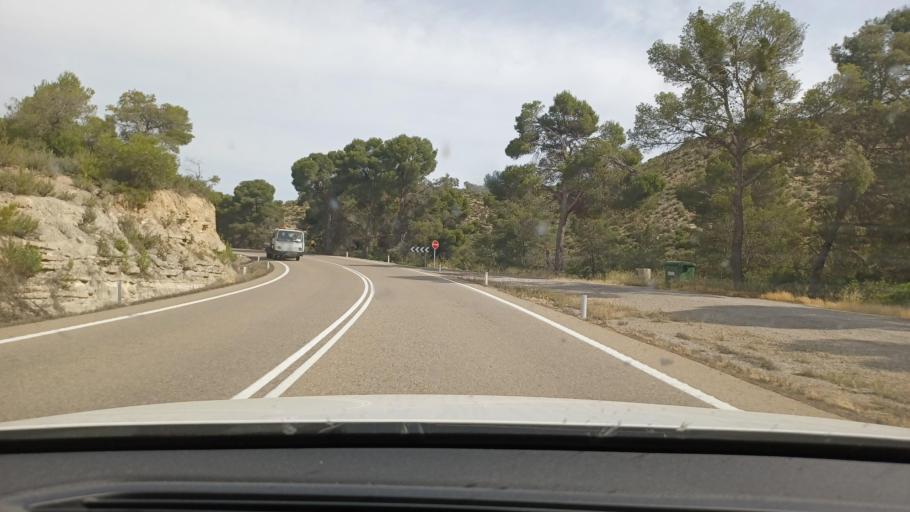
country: ES
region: Aragon
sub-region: Provincia de Zaragoza
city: Chiprana
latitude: 41.3567
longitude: -0.1003
